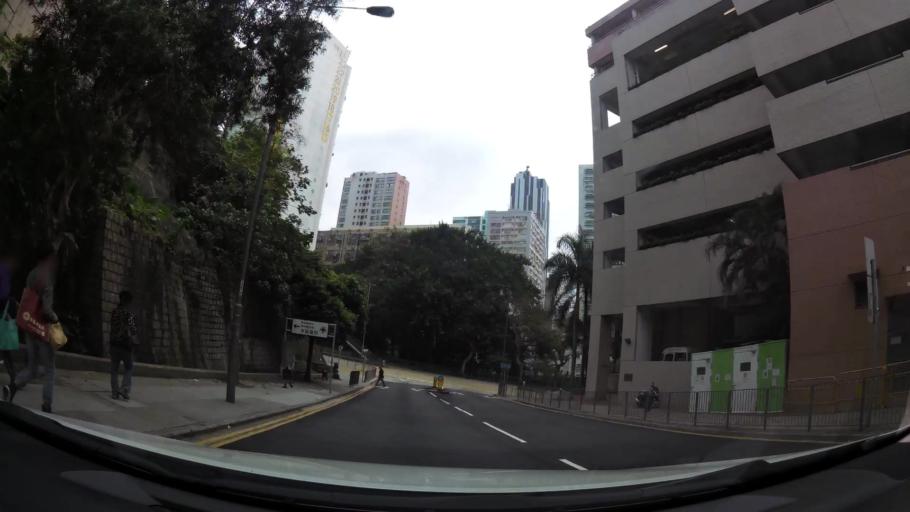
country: HK
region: Wanchai
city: Wan Chai
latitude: 22.2636
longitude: 114.2348
